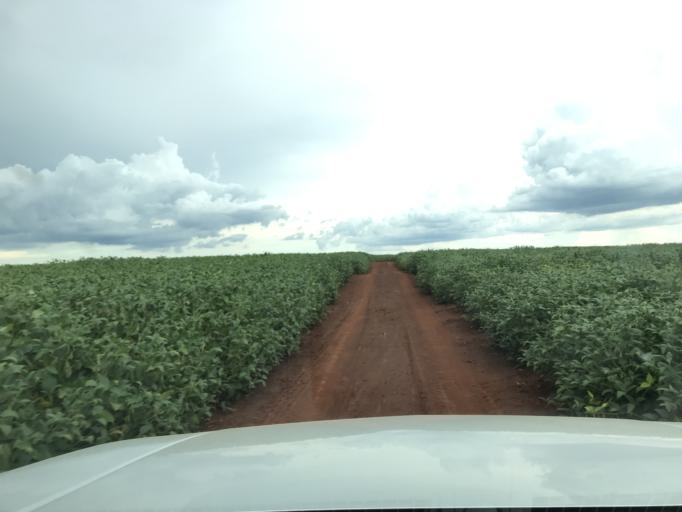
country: BR
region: Parana
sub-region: Palotina
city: Palotina
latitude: -24.2715
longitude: -53.7835
